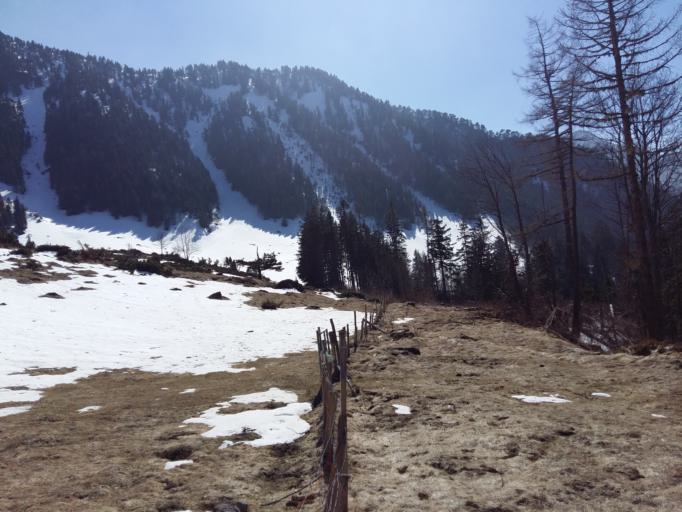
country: FR
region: Midi-Pyrenees
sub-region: Departement des Hautes-Pyrenees
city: Cauterets
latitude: 42.8897
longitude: -0.0917
